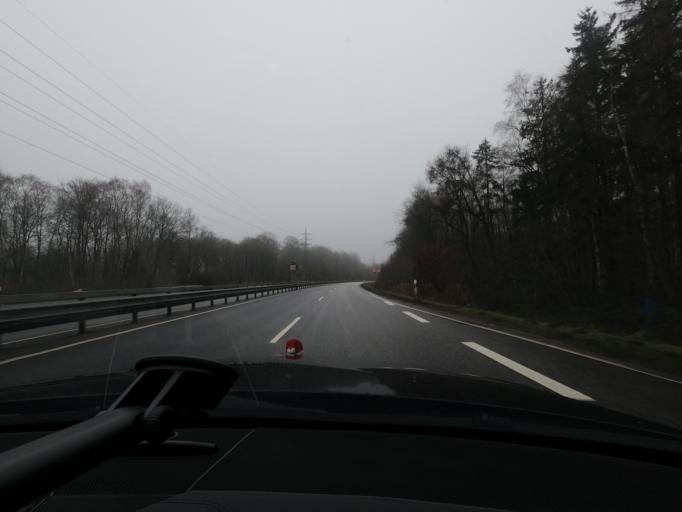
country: DE
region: Schleswig-Holstein
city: Harrislee
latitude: 54.7958
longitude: 9.4094
